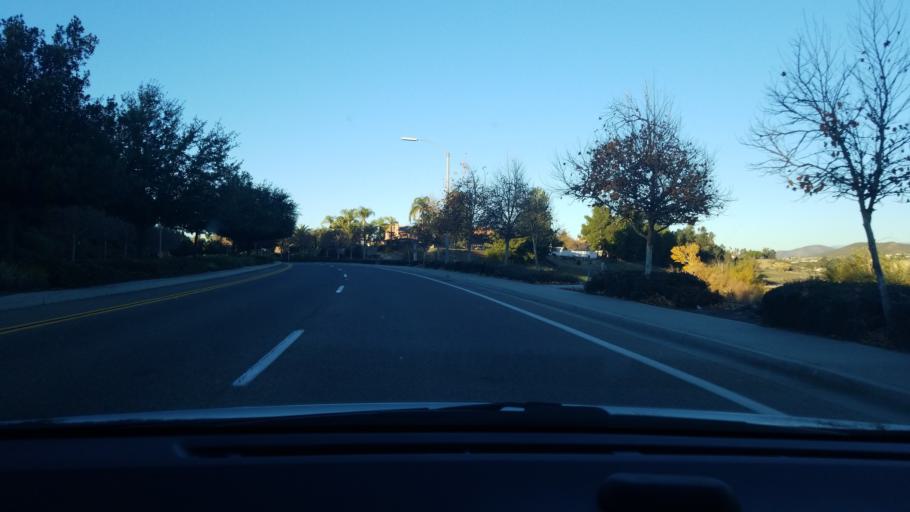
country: US
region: California
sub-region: Riverside County
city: Murrieta Hot Springs
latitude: 33.5382
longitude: -117.1503
